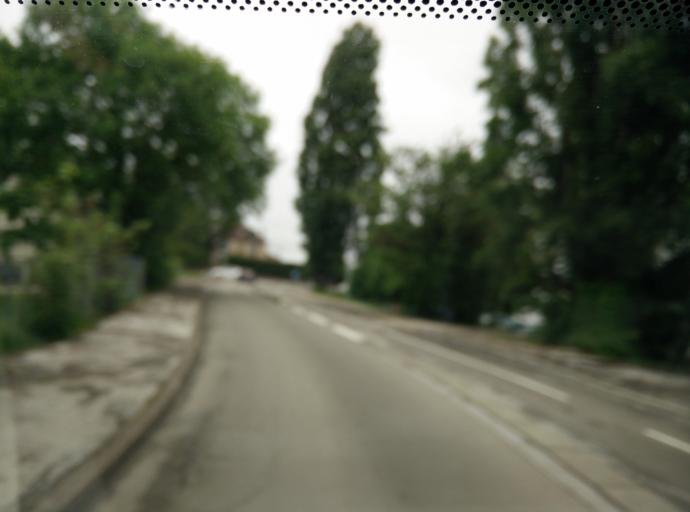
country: FR
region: Franche-Comte
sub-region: Departement du Doubs
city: Beure
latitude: 47.2269
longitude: 5.9827
